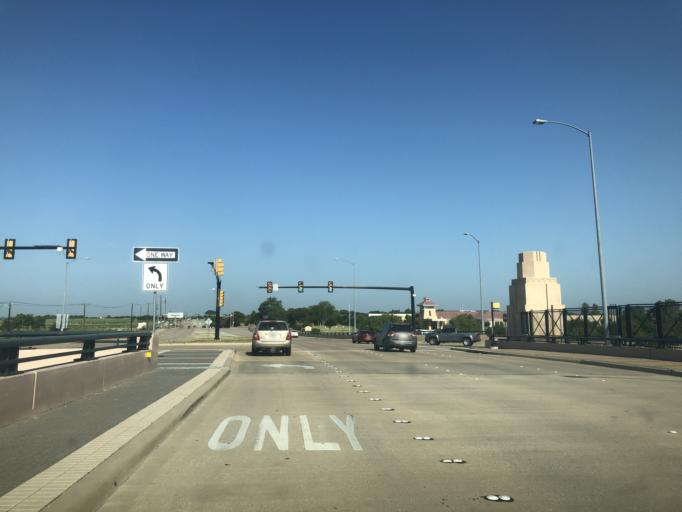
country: US
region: Texas
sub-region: Tarrant County
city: Benbrook
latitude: 32.6454
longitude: -97.4158
